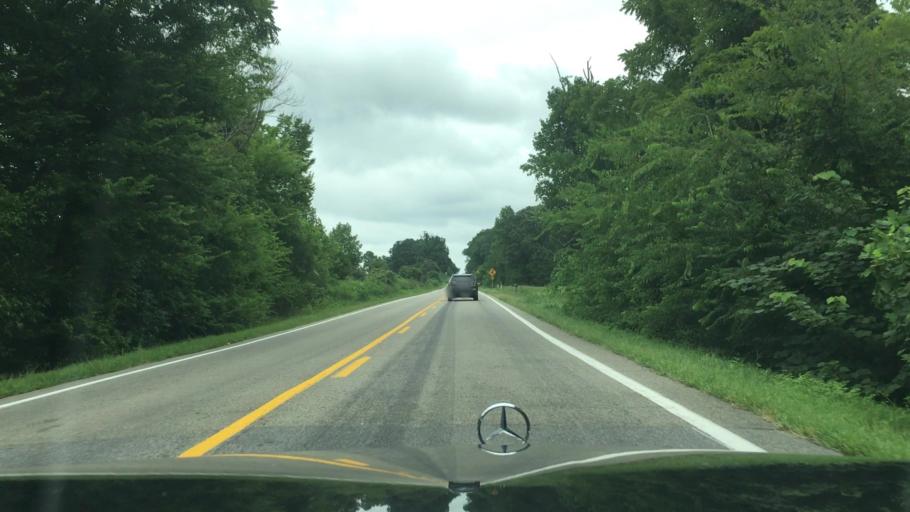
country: US
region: Virginia
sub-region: Prince Edward County
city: Farmville
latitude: 37.2739
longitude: -78.2588
